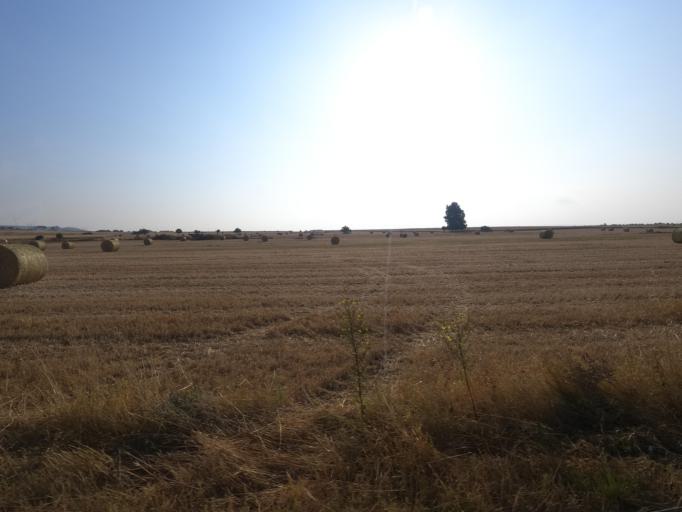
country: CY
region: Larnaka
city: Tersefanou
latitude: 34.8298
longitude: 33.5105
